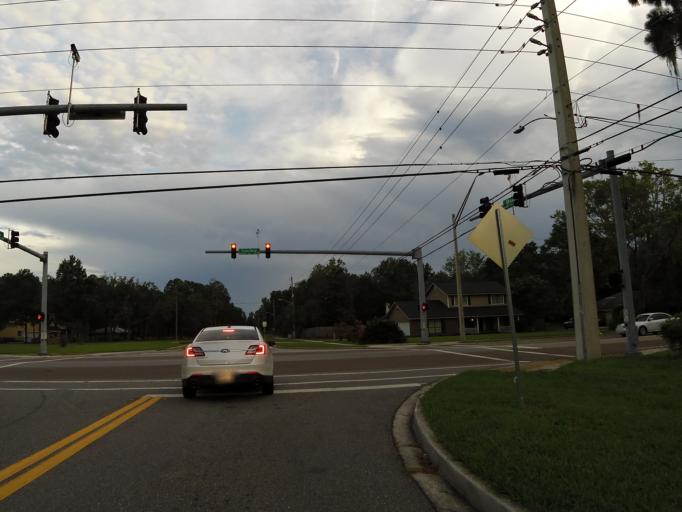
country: US
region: Florida
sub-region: Duval County
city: Baldwin
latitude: 30.3021
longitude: -81.8320
